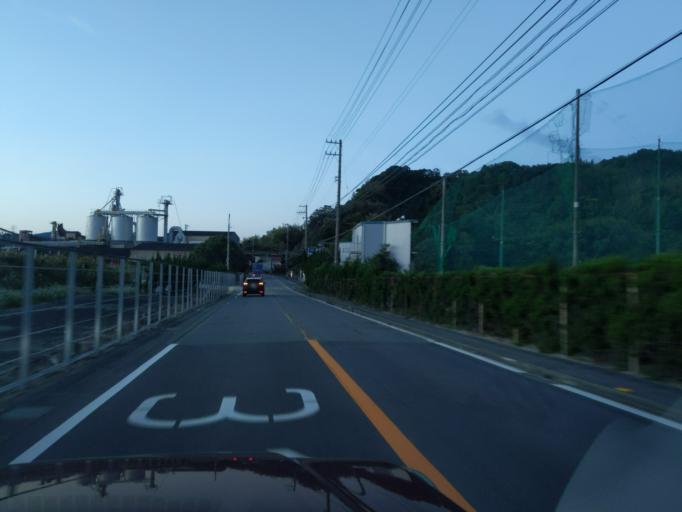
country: JP
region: Tokushima
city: Anan
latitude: 33.8694
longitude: 134.6335
